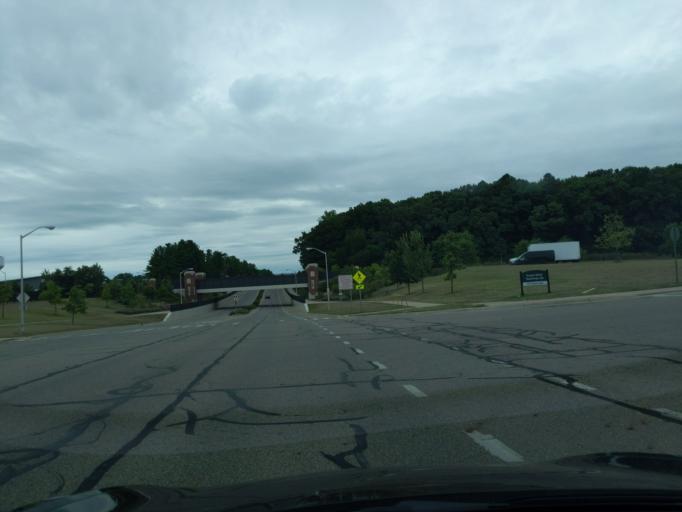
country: US
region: Michigan
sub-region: Ingham County
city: East Lansing
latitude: 42.7128
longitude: -84.4782
